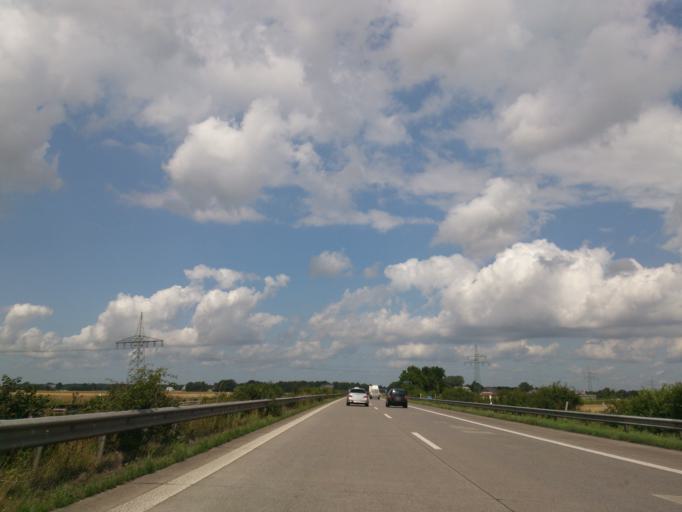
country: DE
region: Schleswig-Holstein
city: Rethwisch
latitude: 53.8556
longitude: 9.5788
